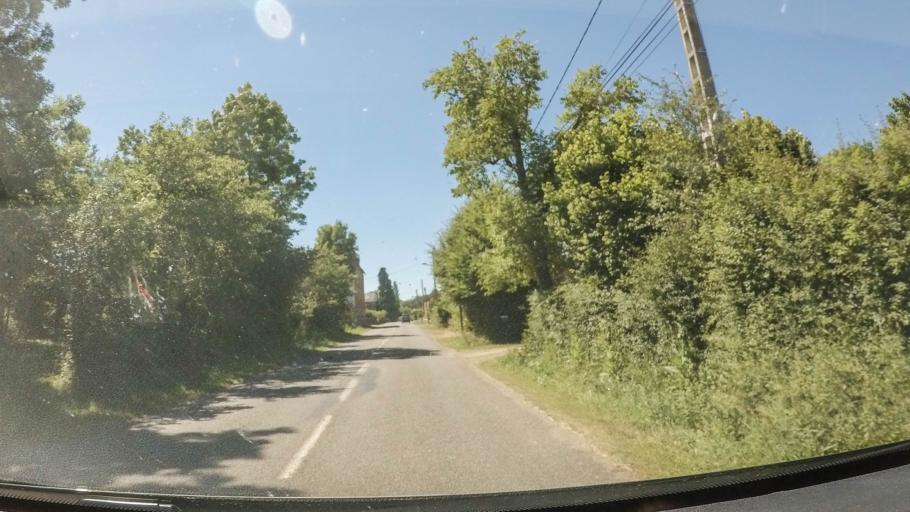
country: FR
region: Midi-Pyrenees
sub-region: Departement de l'Aveyron
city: Saint-Christophe-Vallon
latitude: 44.4629
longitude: 2.3892
